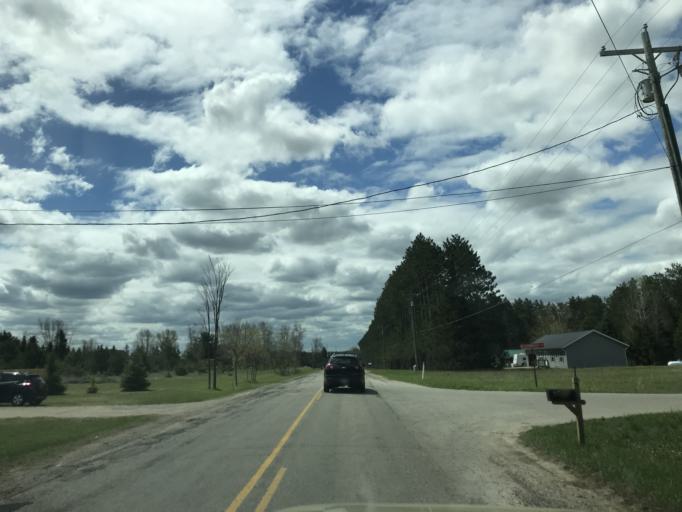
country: US
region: Michigan
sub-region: Otsego County
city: Gaylord
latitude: 45.0400
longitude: -84.6942
